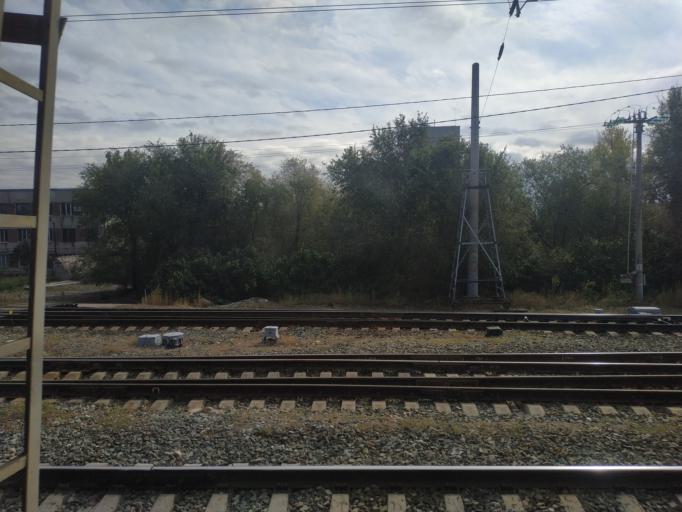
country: RU
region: Volgograd
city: Volgograd
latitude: 48.6668
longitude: 44.4590
